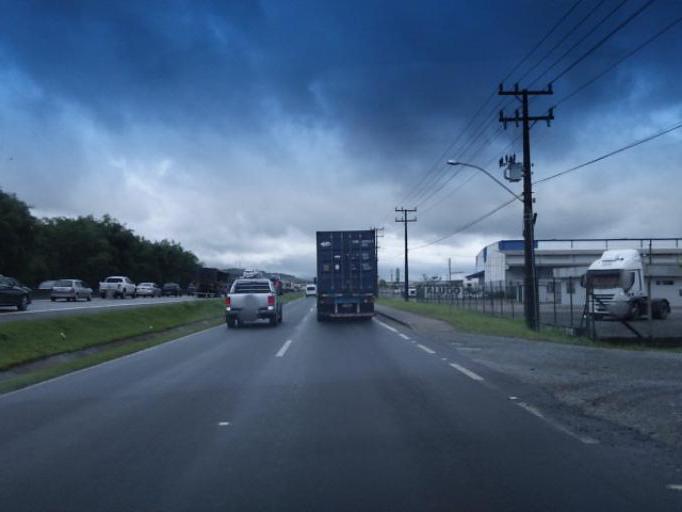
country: BR
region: Santa Catarina
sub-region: Itajai
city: Itajai
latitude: -26.9263
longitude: -48.7061
